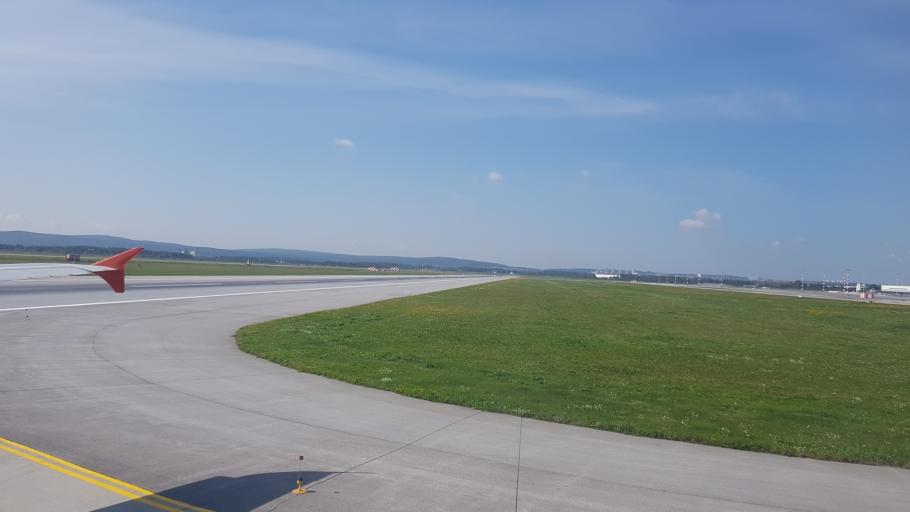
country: RU
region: Sverdlovsk
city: Istok
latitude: 56.7453
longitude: 60.8065
